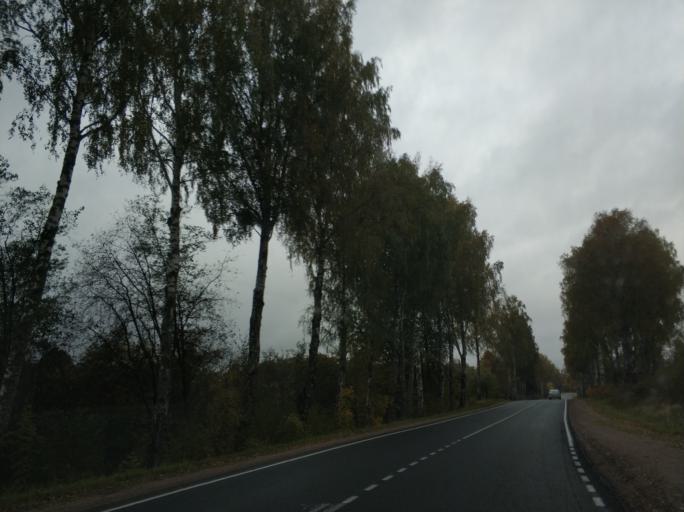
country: RU
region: Pskov
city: Opochka
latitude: 56.5508
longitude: 28.6341
